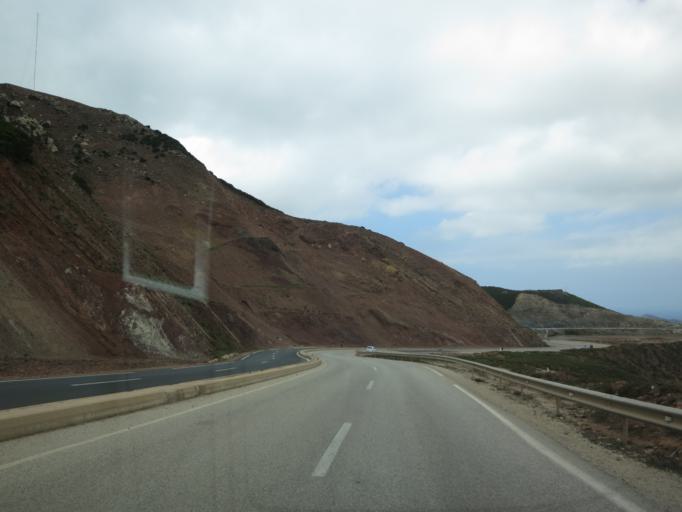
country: ES
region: Ceuta
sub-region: Ceuta
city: Ceuta
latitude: 35.8538
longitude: -5.4369
